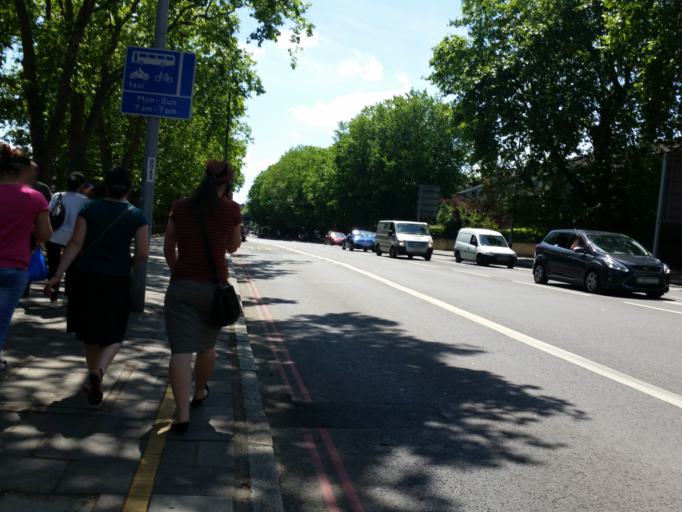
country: GB
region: England
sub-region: Greater London
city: Harringay
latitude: 51.5827
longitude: -0.0722
